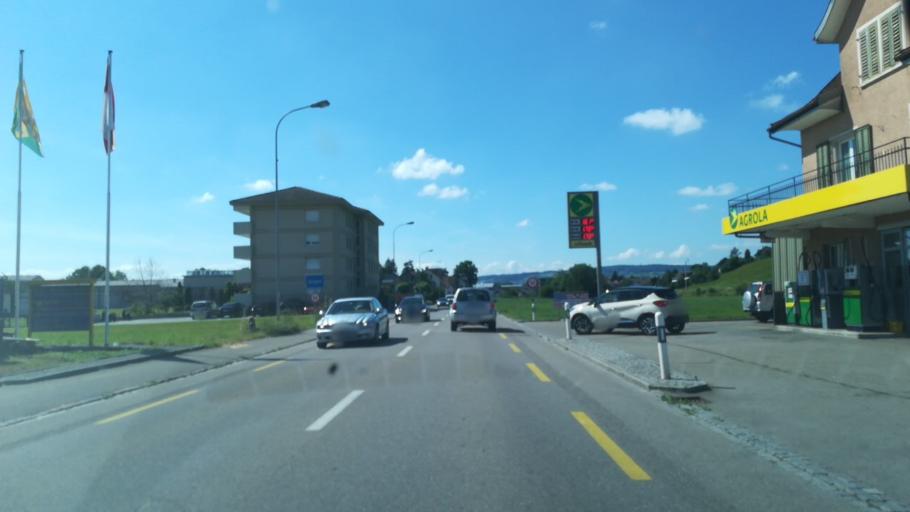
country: CH
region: Thurgau
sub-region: Weinfelden District
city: Sulgen
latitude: 47.5294
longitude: 9.1932
